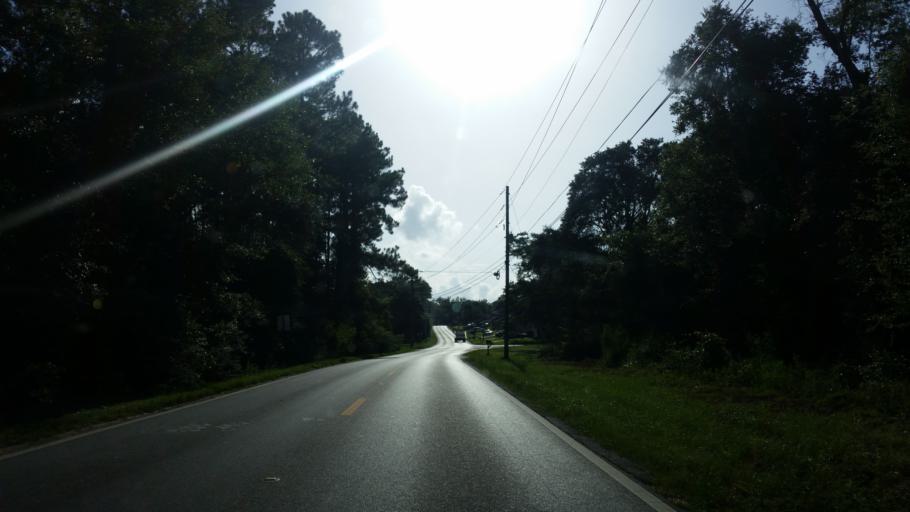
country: US
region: Florida
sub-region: Santa Rosa County
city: Bagdad
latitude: 30.5799
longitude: -87.0427
